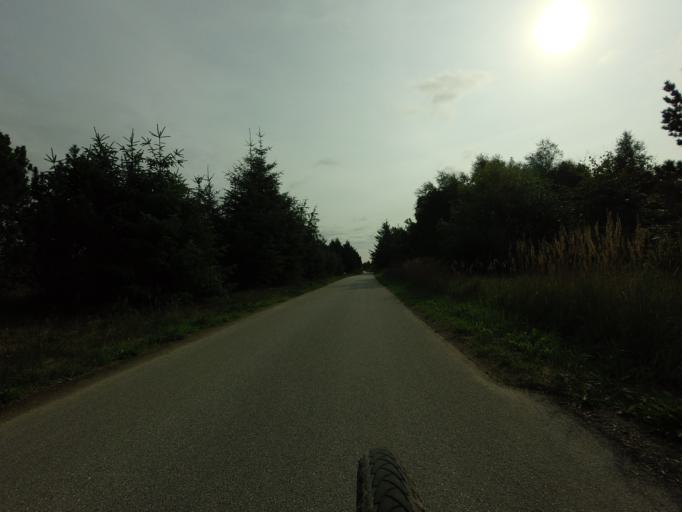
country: DK
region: North Denmark
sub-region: Hjorring Kommune
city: Sindal
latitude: 57.5861
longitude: 10.1512
